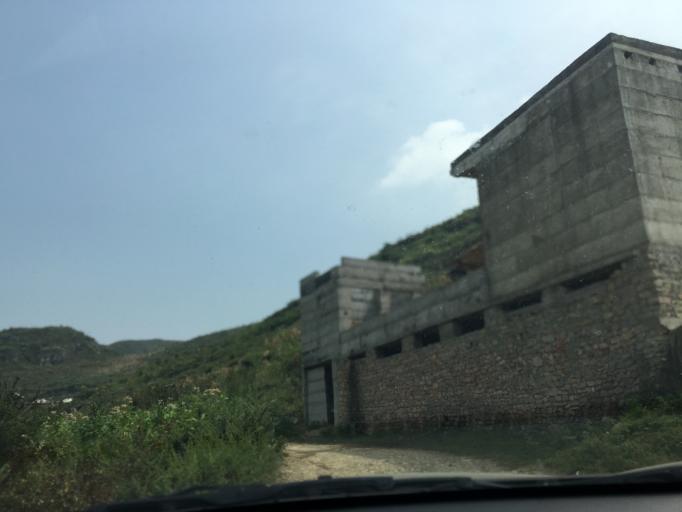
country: CN
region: Guizhou Sheng
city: Anshun
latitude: 25.5984
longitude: 105.6662
